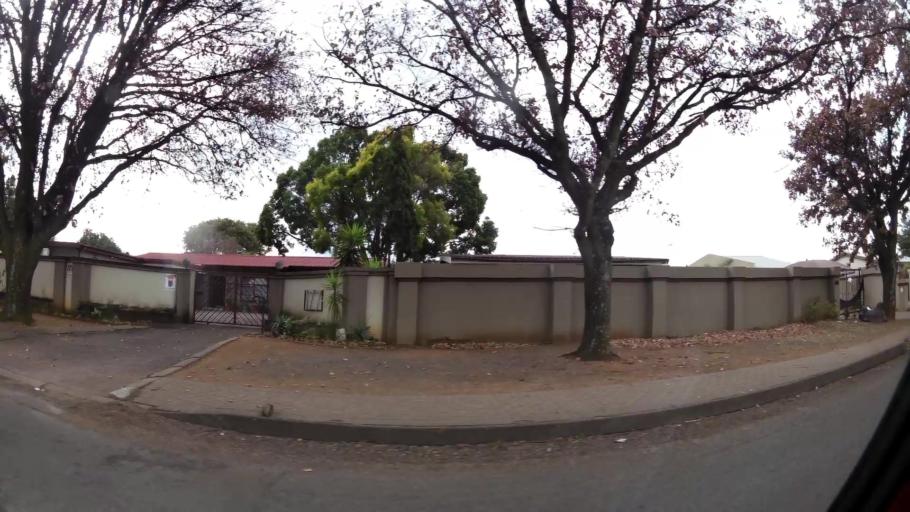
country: ZA
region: Gauteng
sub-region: Sedibeng District Municipality
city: Vanderbijlpark
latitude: -26.7223
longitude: 27.8388
